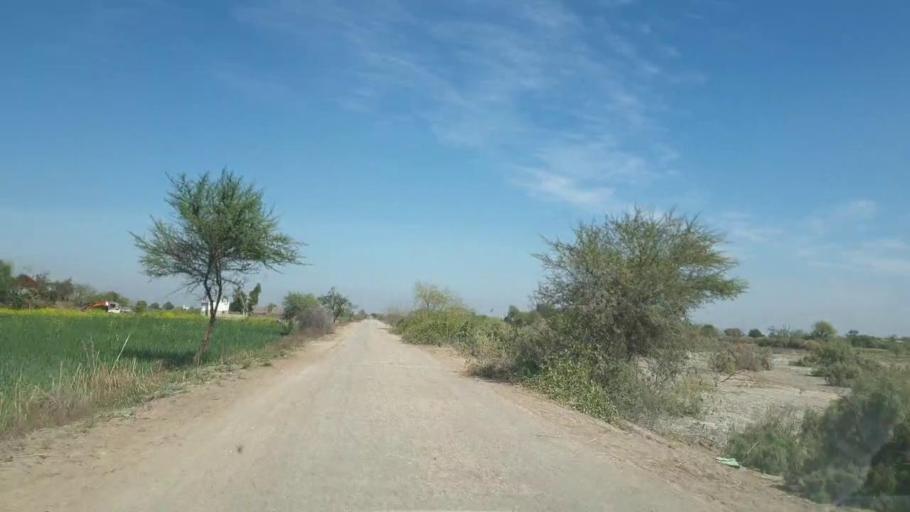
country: PK
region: Sindh
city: Pithoro
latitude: 25.6309
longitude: 69.2180
